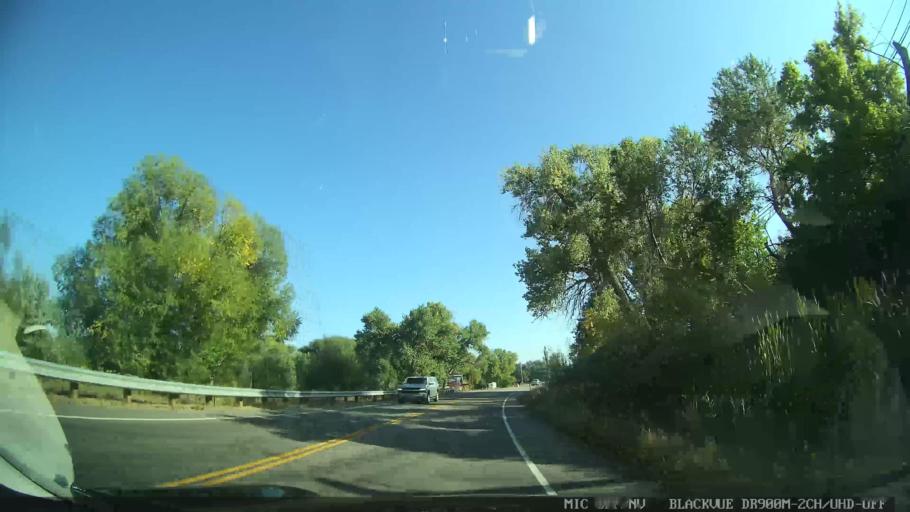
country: US
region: Colorado
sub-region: Larimer County
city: Loveland
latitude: 40.4145
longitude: -105.1701
